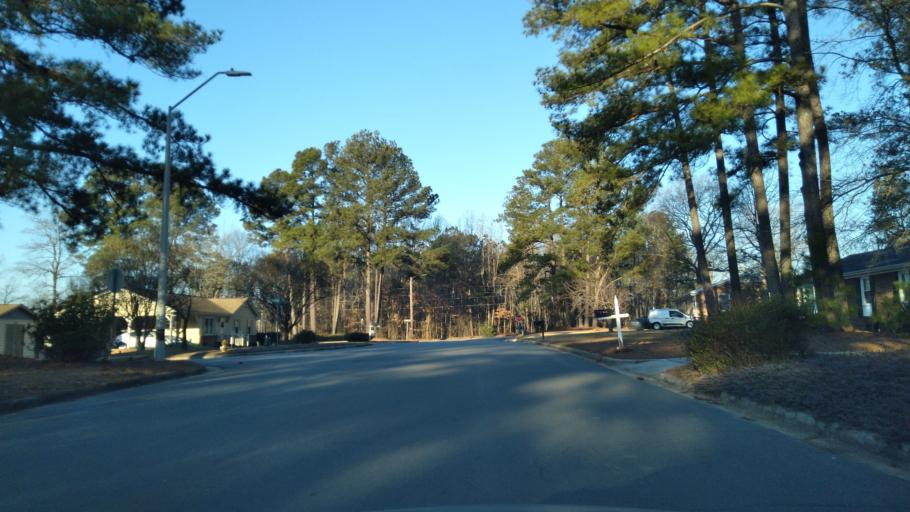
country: US
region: North Carolina
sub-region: Wake County
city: Garner
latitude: 35.6875
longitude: -78.6135
